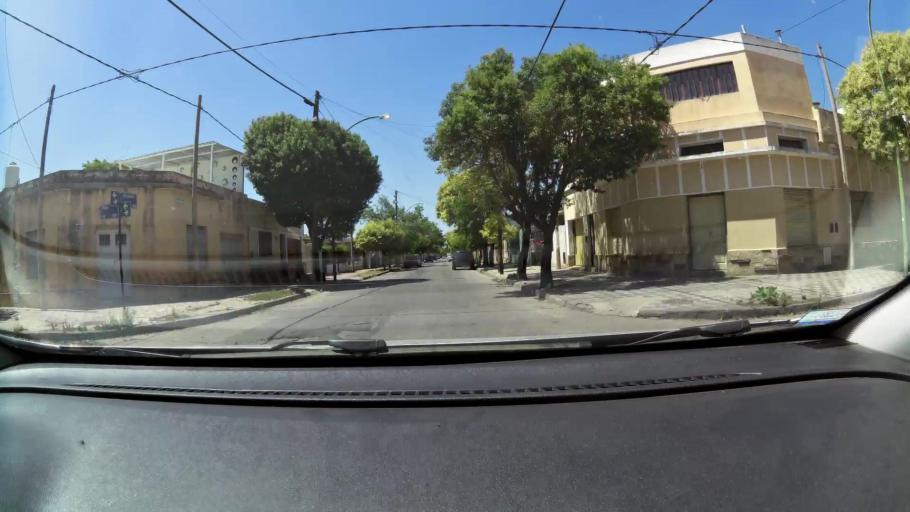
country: AR
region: Cordoba
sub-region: Departamento de Capital
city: Cordoba
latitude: -31.3867
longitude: -64.1550
